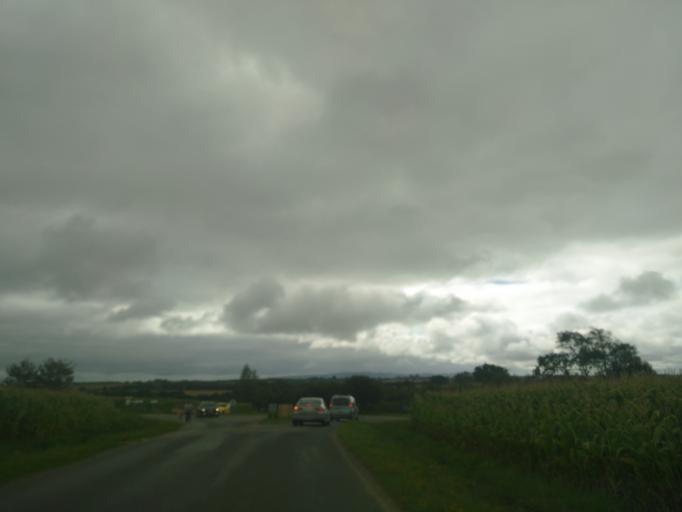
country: FR
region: Brittany
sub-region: Departement du Finistere
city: Plomodiern
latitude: 48.1567
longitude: -4.2457
